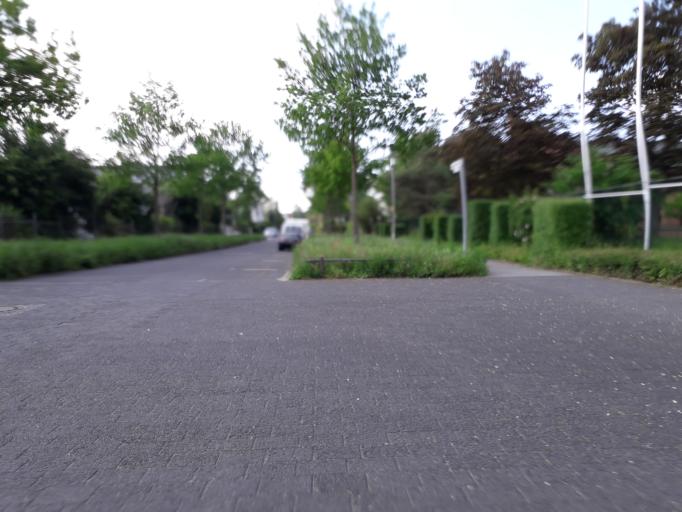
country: DE
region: Hesse
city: Pfungstadt
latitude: 49.8142
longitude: 8.6361
